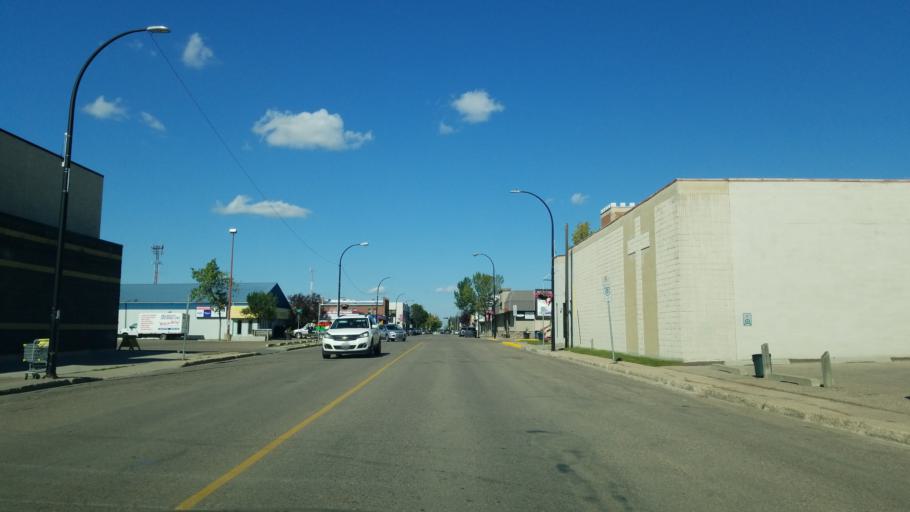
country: CA
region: Saskatchewan
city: Lloydminster
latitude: 53.2809
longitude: -110.0035
